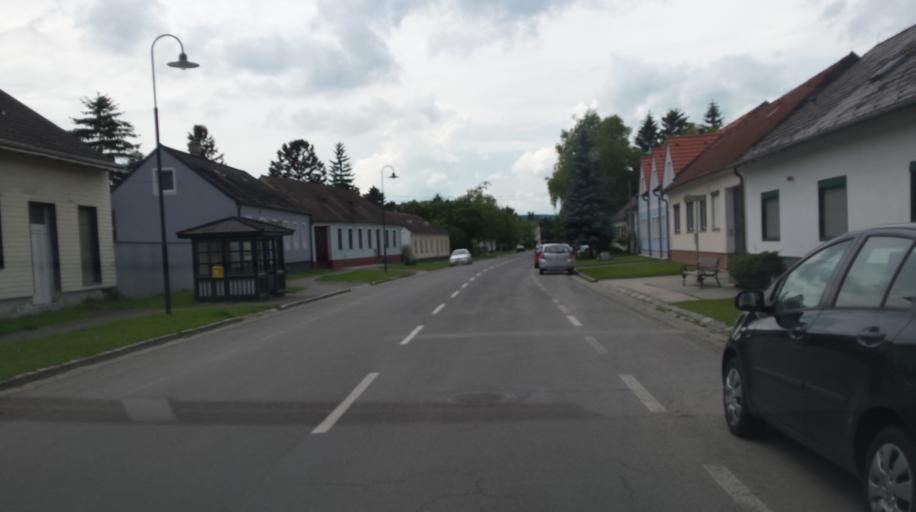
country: AT
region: Lower Austria
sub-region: Politischer Bezirk Mistelbach
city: Wolkersdorf im Weinviertel
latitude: 48.4102
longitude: 16.5146
